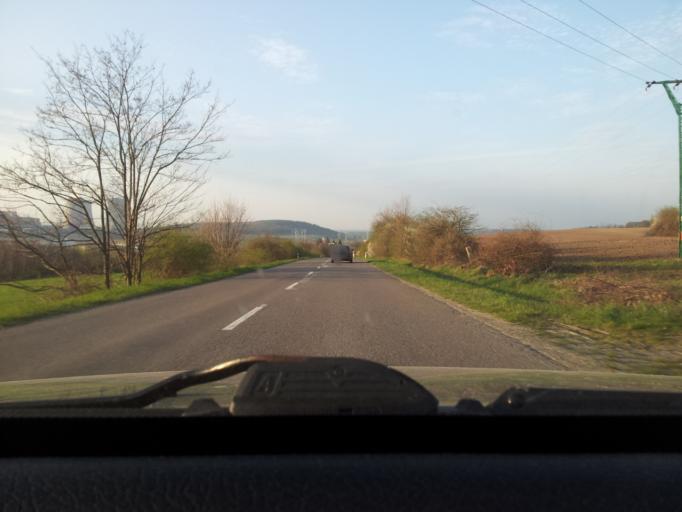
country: SK
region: Nitriansky
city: Tlmace
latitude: 48.2747
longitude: 18.4471
